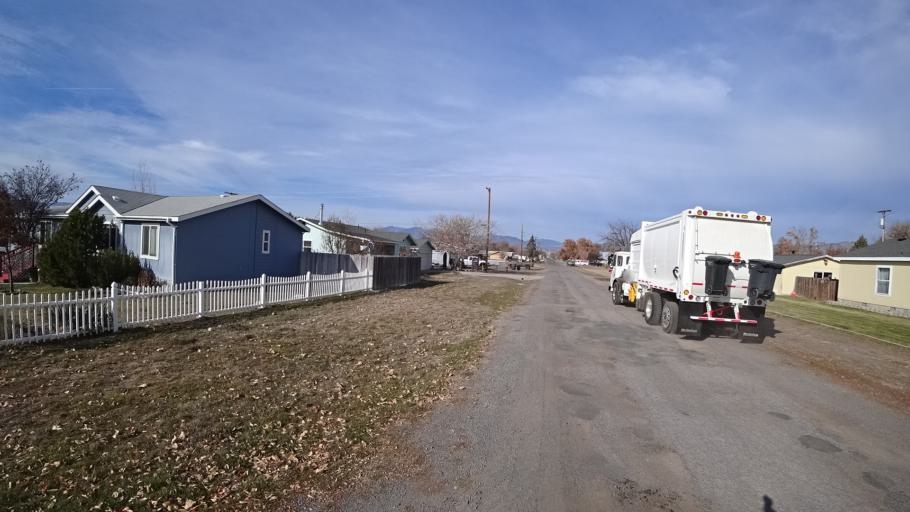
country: US
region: California
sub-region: Siskiyou County
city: Montague
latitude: 41.7249
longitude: -122.5231
